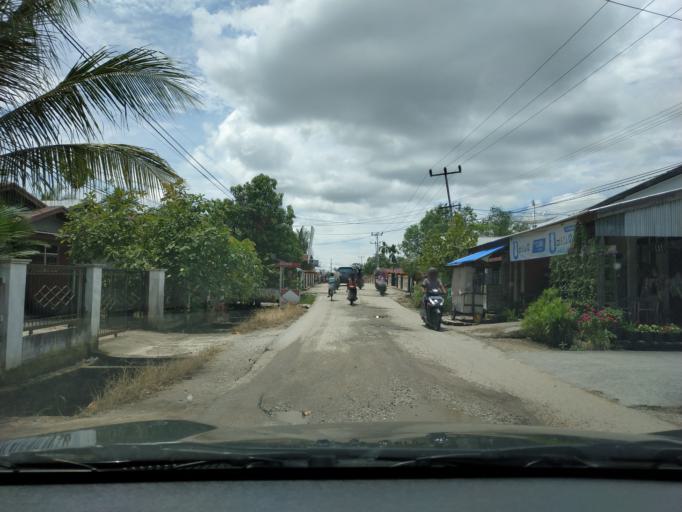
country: ID
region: Riau
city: Tembilahan
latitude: -0.3176
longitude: 103.1675
